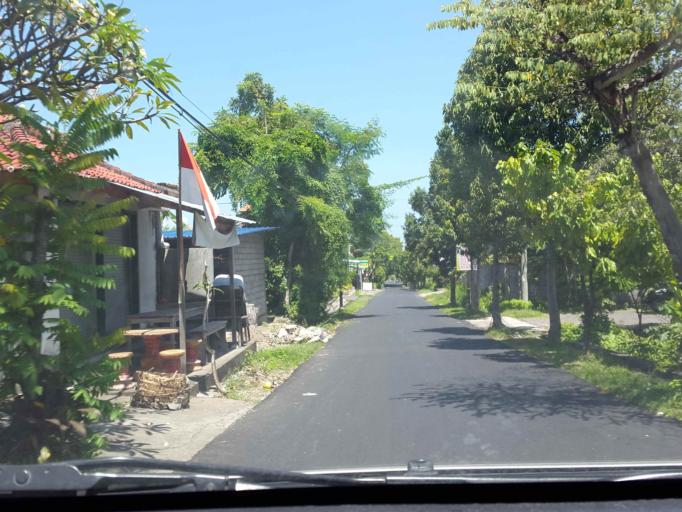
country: ID
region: Bali
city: Semarapura
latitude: -8.5403
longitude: 115.4056
